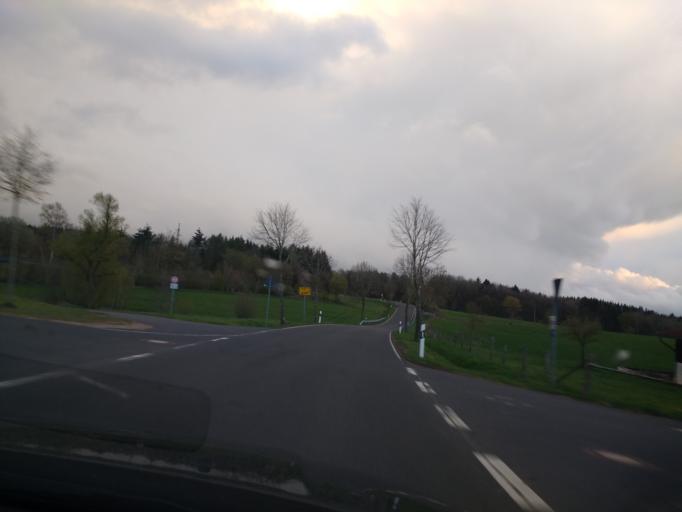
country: DE
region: Rheinland-Pfalz
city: Wiesbaum
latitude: 50.3379
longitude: 6.6689
